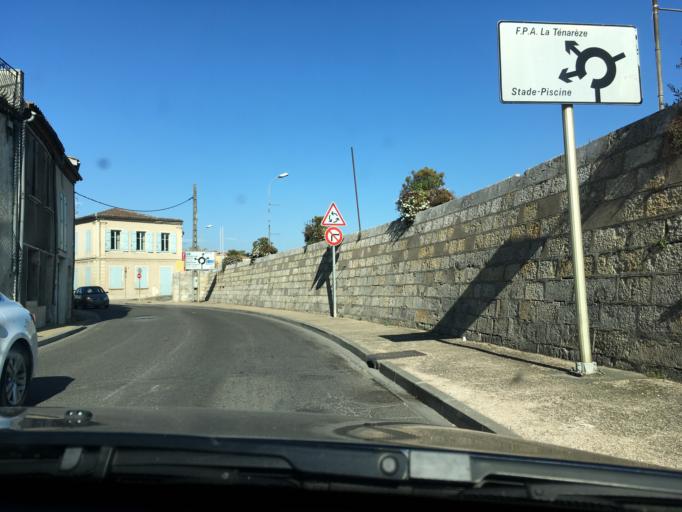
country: FR
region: Midi-Pyrenees
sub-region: Departement du Gers
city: Condom
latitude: 43.9574
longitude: 0.3683
